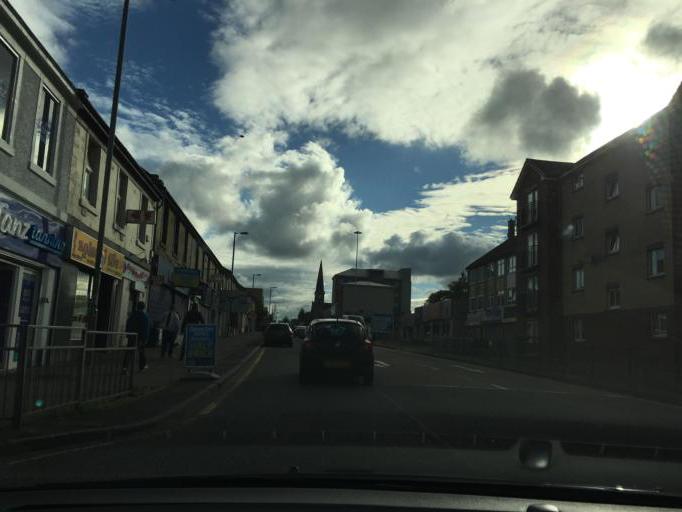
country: GB
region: Scotland
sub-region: North Lanarkshire
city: Motherwell
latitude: 55.7930
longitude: -3.9879
